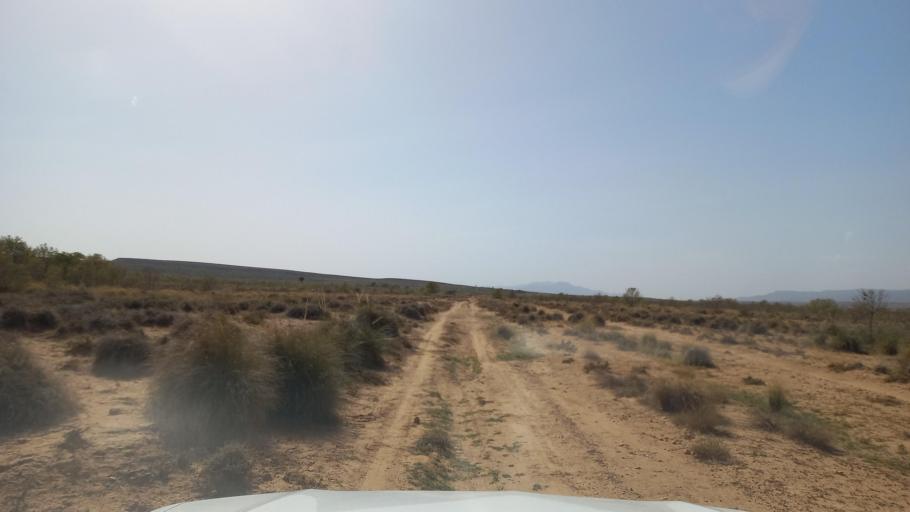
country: TN
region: Al Qasrayn
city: Kasserine
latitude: 35.2149
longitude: 9.0128
